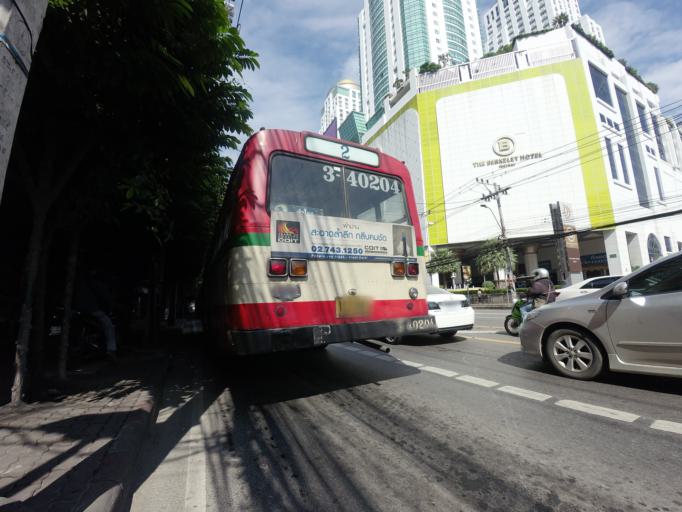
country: TH
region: Bangkok
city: Ratchathewi
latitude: 13.7495
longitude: 100.5432
